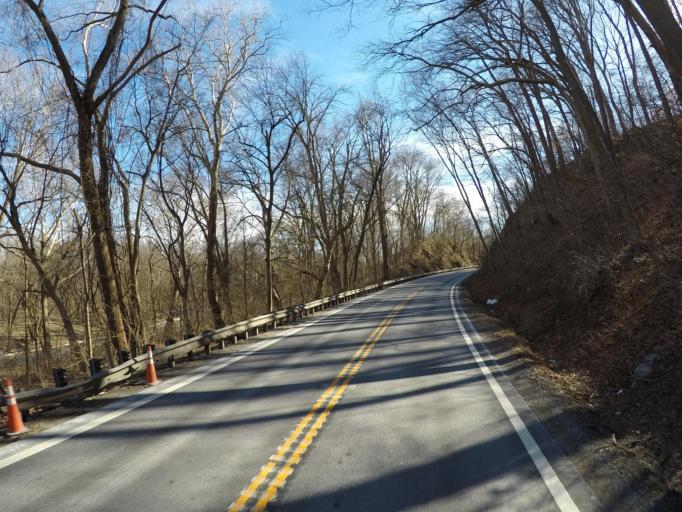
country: US
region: Maryland
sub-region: Frederick County
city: Point of Rocks
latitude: 39.2676
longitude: -77.5450
